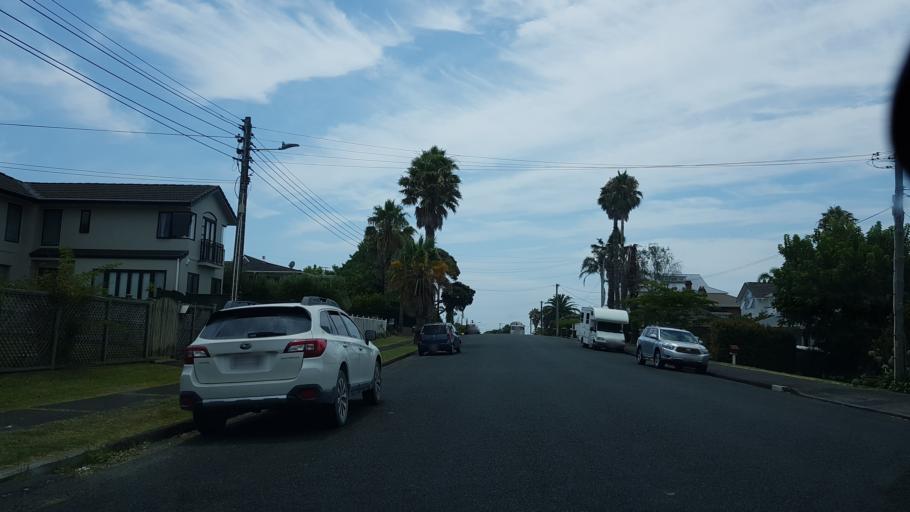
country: NZ
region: Auckland
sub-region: Auckland
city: North Shore
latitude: -36.7994
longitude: 174.7788
